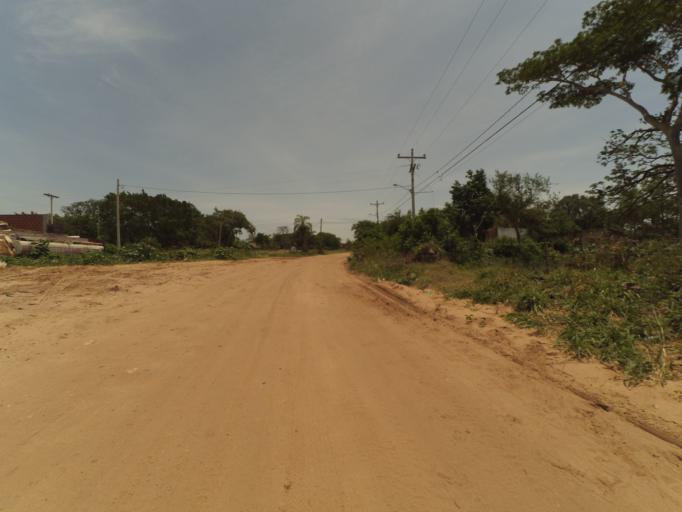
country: BO
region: Santa Cruz
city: Santa Cruz de la Sierra
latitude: -17.8299
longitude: -63.2524
